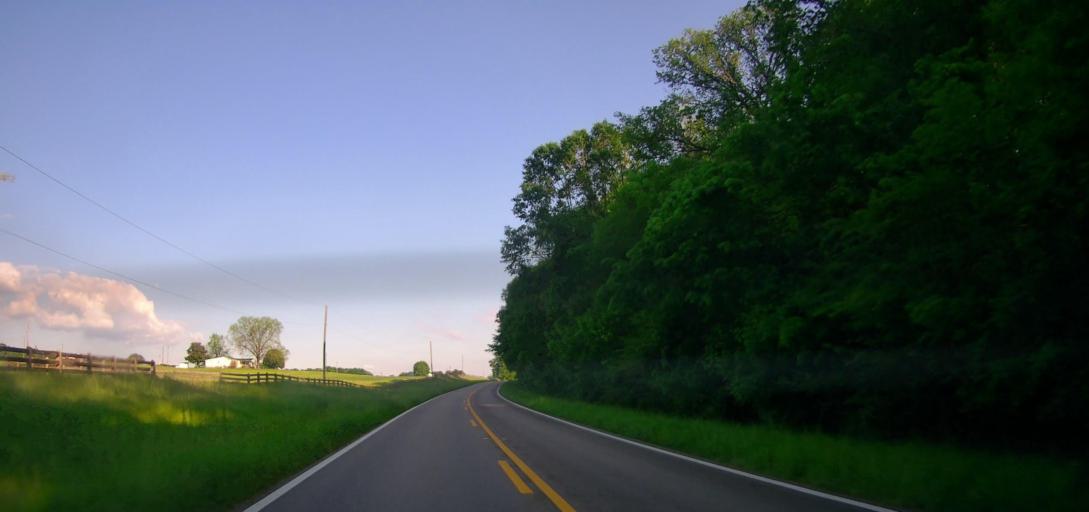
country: US
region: Georgia
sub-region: Putnam County
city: Eatonton
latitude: 33.2994
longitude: -83.3370
